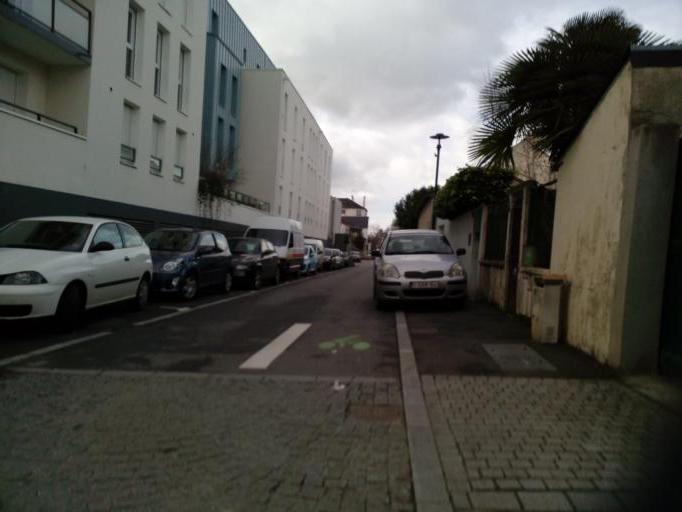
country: FR
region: Brittany
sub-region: Departement d'Ille-et-Vilaine
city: Rennes
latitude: 48.1085
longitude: -1.7031
